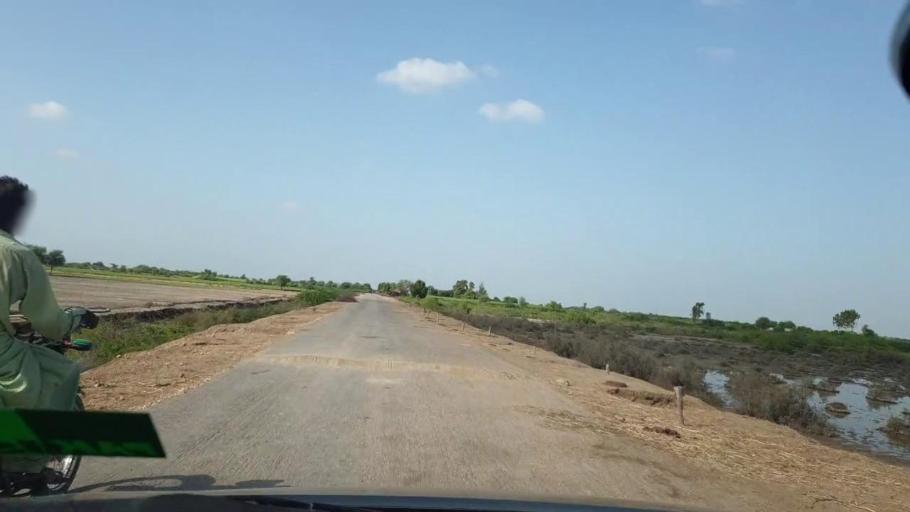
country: PK
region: Sindh
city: Tando Bago
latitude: 24.7062
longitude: 69.1920
